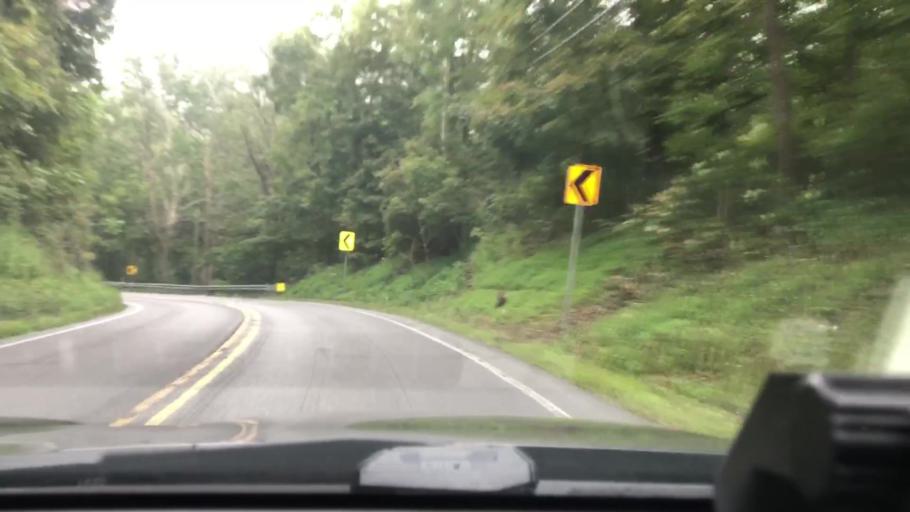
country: US
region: Pennsylvania
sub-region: Berks County
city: Kutztown
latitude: 40.5378
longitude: -75.7996
